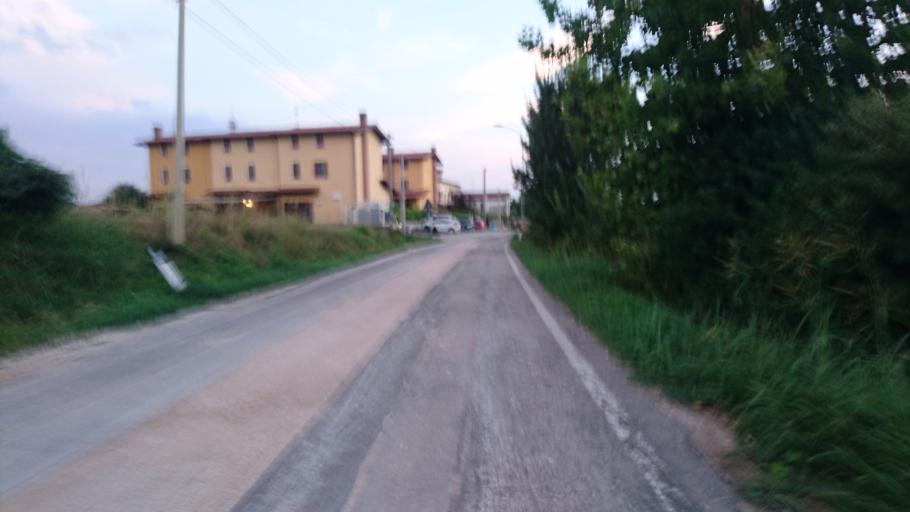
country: IT
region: Veneto
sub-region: Provincia di Padova
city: Tencarola
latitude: 45.3832
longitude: 11.8070
